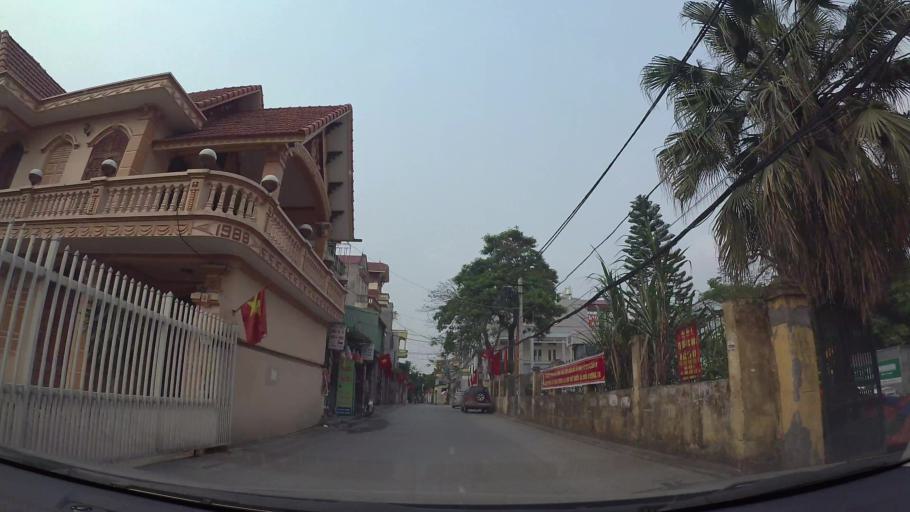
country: VN
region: Ha Noi
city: Trau Quy
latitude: 21.0724
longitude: 105.9008
